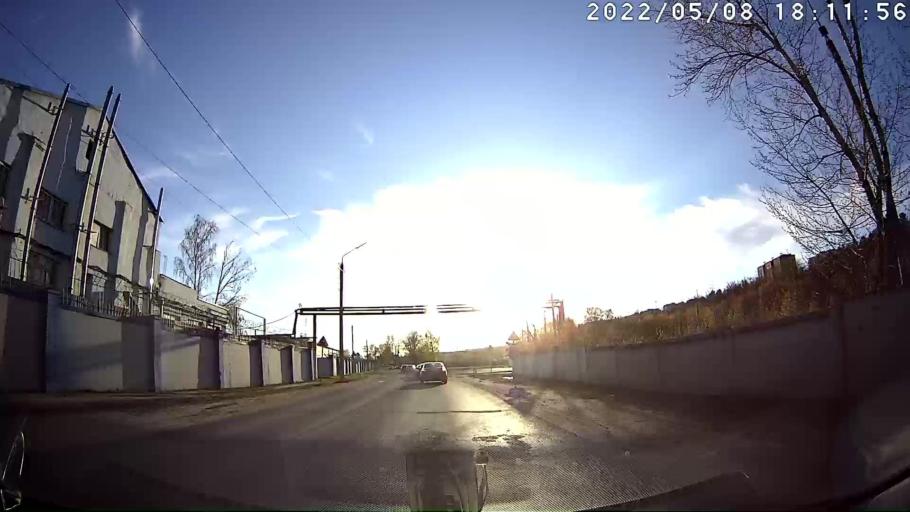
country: RU
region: Tatarstan
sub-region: Zelenodol'skiy Rayon
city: Zelenodolsk
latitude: 55.8407
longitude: 48.5061
